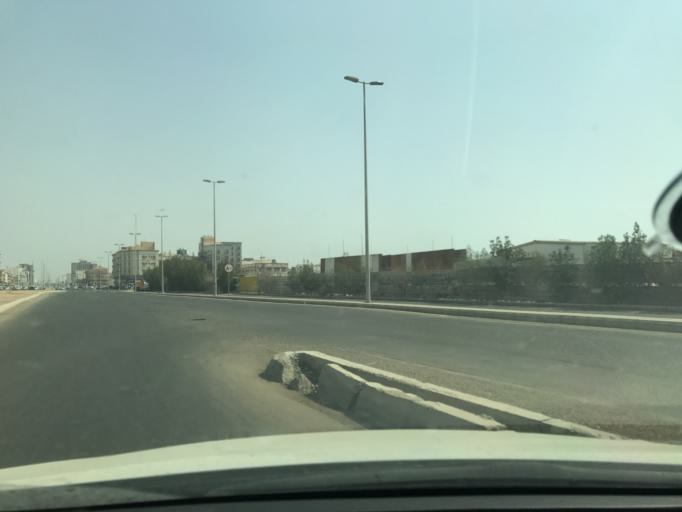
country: SA
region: Makkah
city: Jeddah
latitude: 21.6335
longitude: 39.1601
